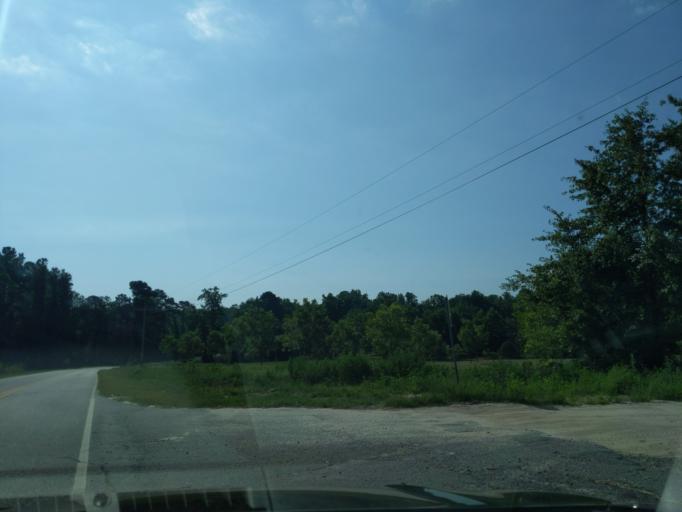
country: US
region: South Carolina
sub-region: Lexington County
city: Leesville
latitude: 33.9134
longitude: -81.4405
